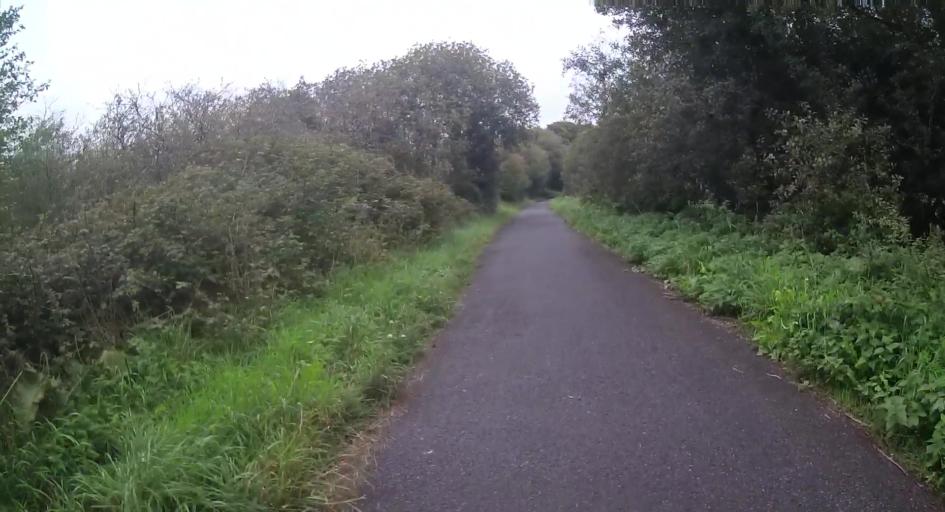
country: GB
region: England
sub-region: Isle of Wight
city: Newchurch
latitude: 50.6706
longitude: -1.2063
